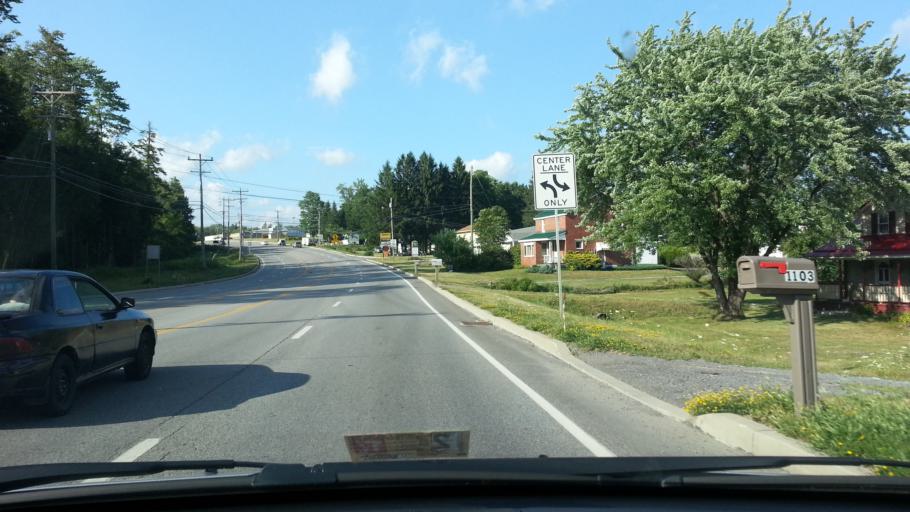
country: US
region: Pennsylvania
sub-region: Elk County
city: Saint Marys
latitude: 41.3911
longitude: -78.5576
